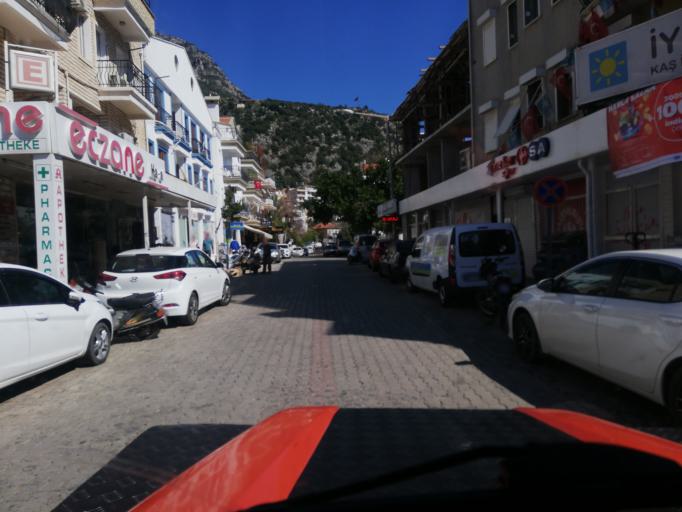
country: TR
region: Antalya
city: Kas
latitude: 36.2016
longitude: 29.6387
